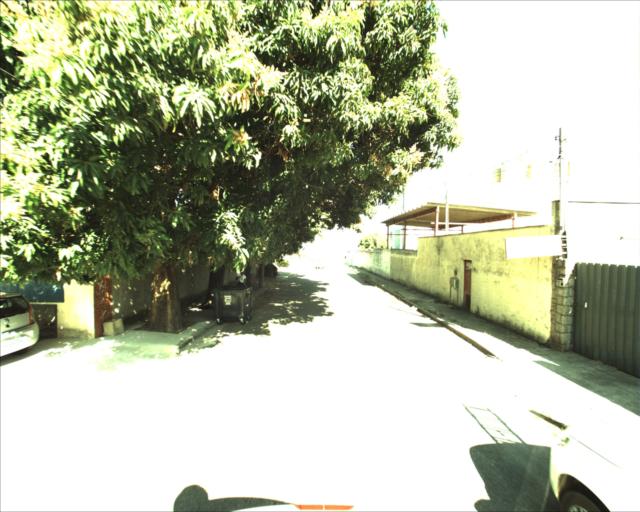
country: BR
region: Sao Paulo
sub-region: Sorocaba
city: Sorocaba
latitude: -23.4906
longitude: -47.4274
